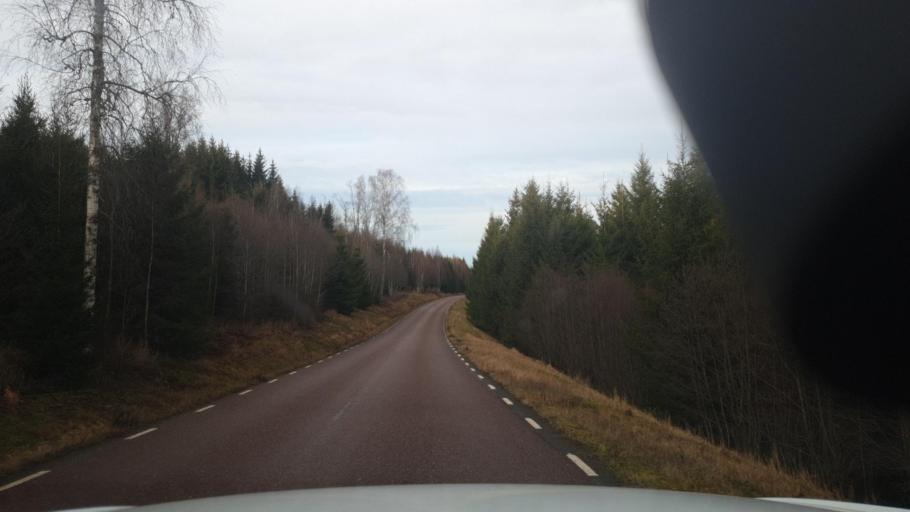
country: NO
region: Ostfold
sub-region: Romskog
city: Romskog
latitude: 59.7222
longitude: 12.0678
